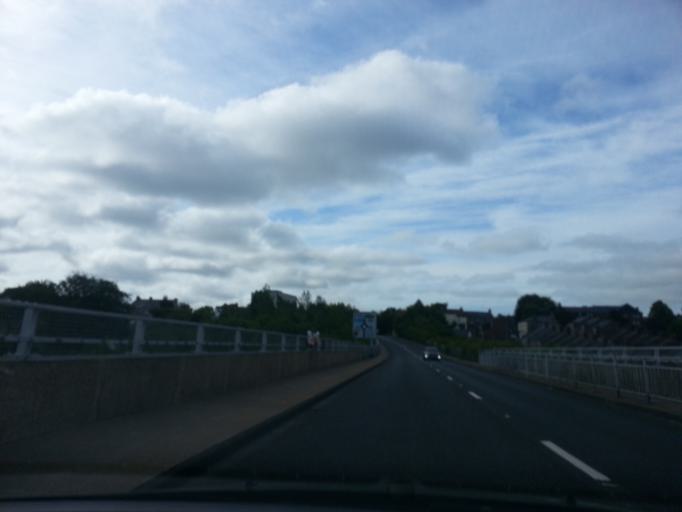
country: GB
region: England
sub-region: County Durham
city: Bishop Auckland
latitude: 54.6667
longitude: -1.6815
